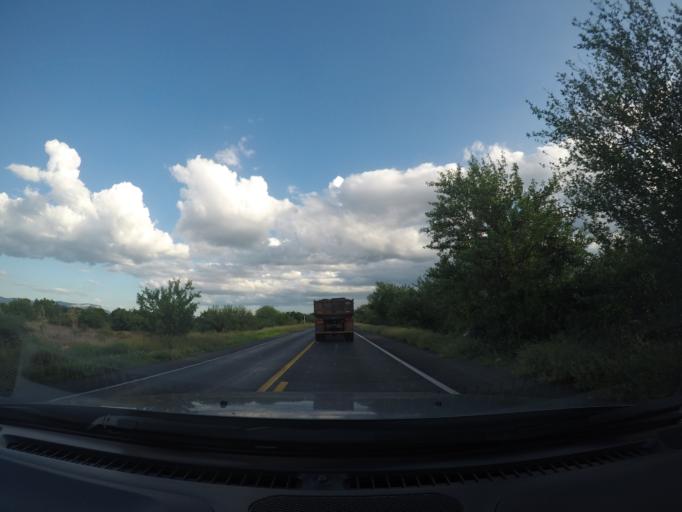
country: BR
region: Bahia
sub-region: Oliveira Dos Brejinhos
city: Beira Rio
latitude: -12.2380
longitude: -42.7738
